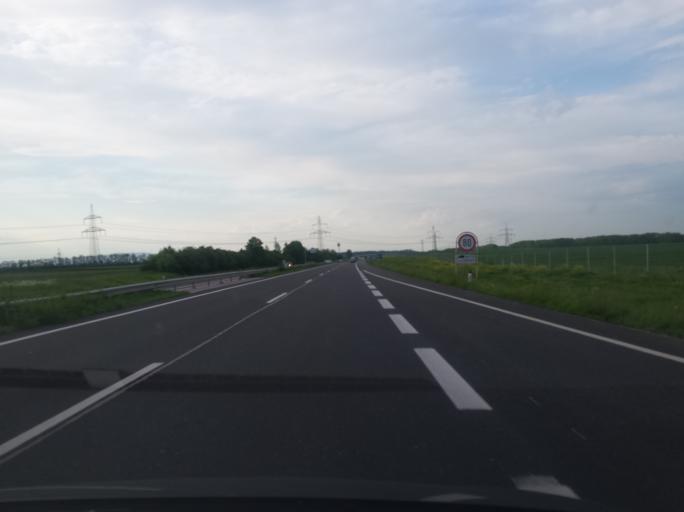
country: AT
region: Burgenland
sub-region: Eisenstadt-Umgebung
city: Hornstein
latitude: 47.8688
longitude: 16.4184
